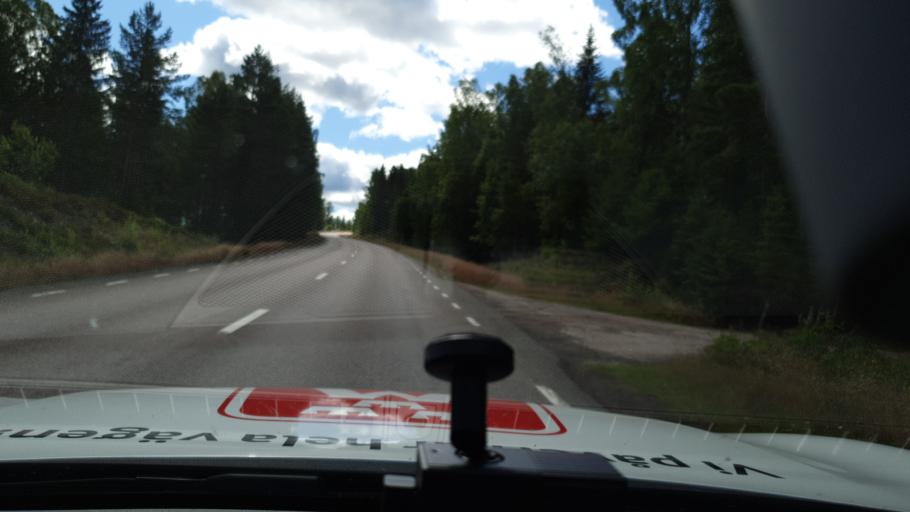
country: SE
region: Vaermland
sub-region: Sunne Kommun
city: Sunne
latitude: 59.7046
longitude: 13.1060
